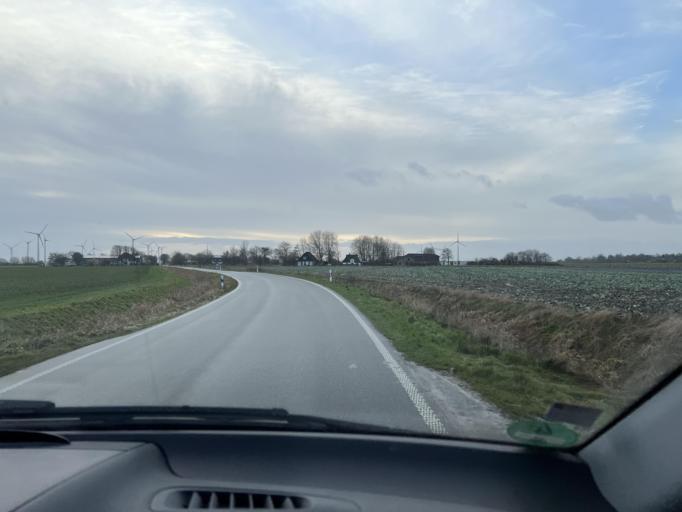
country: DE
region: Schleswig-Holstein
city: Hillgroven
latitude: 54.1929
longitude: 8.8887
